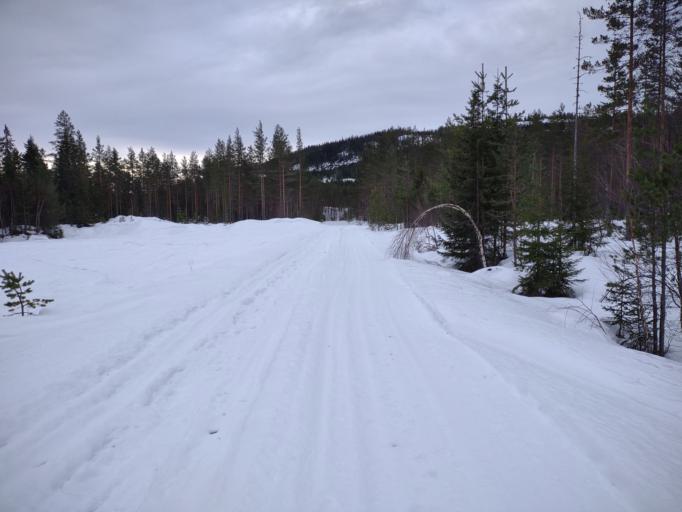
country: NO
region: Buskerud
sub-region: Flesberg
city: Lampeland
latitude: 59.7263
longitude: 9.5373
